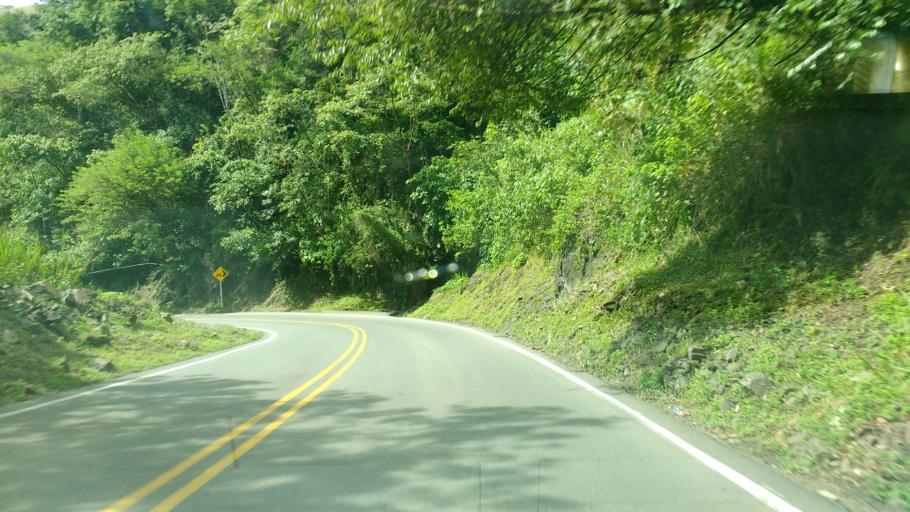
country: CO
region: Antioquia
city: Titiribi
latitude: 6.0019
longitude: -75.7915
